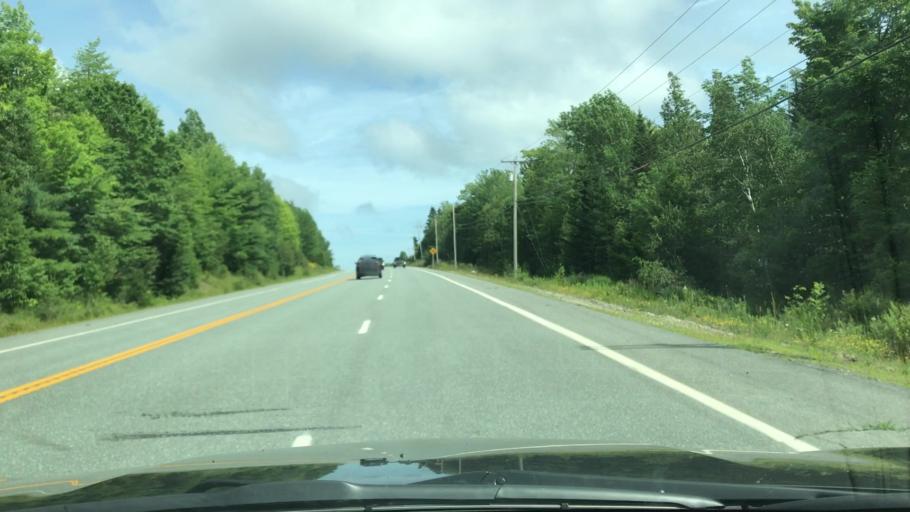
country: US
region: Maine
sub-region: Hancock County
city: Surry
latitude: 44.5479
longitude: -68.5249
